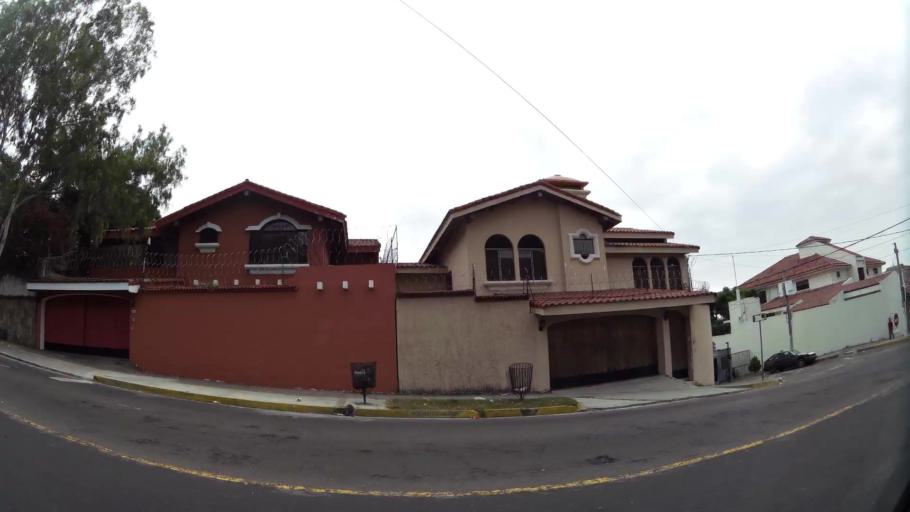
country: SV
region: San Salvador
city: Mejicanos
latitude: 13.7173
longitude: -89.2455
